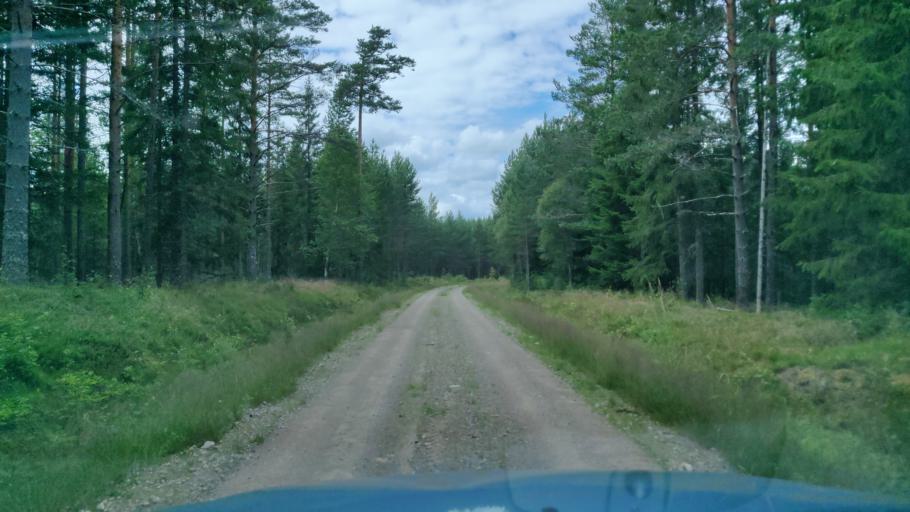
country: SE
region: Vaermland
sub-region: Hagfors Kommun
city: Hagfors
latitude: 59.9509
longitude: 13.5922
